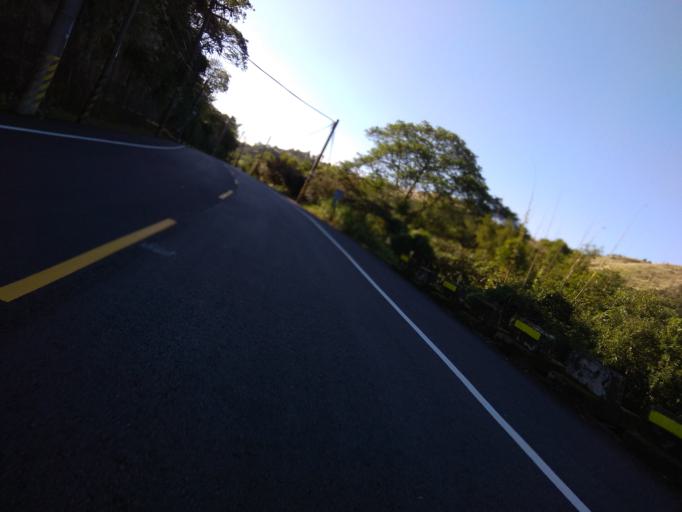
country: TW
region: Taiwan
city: Daxi
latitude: 24.8931
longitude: 121.1454
